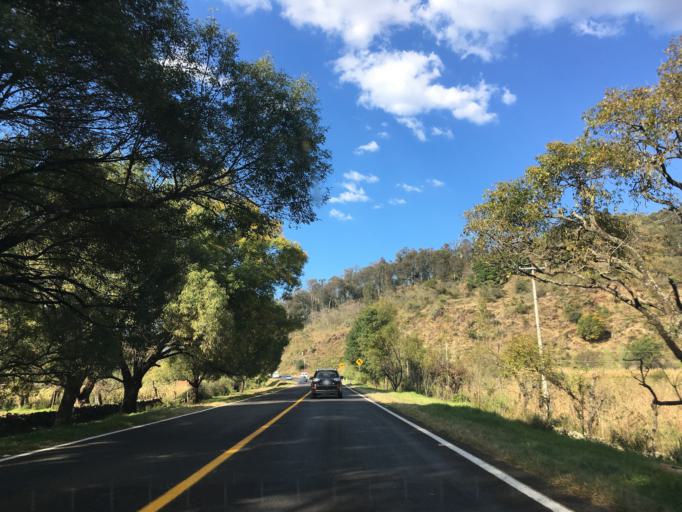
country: MX
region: Michoacan
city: Patzcuaro
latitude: 19.5542
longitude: -101.5799
